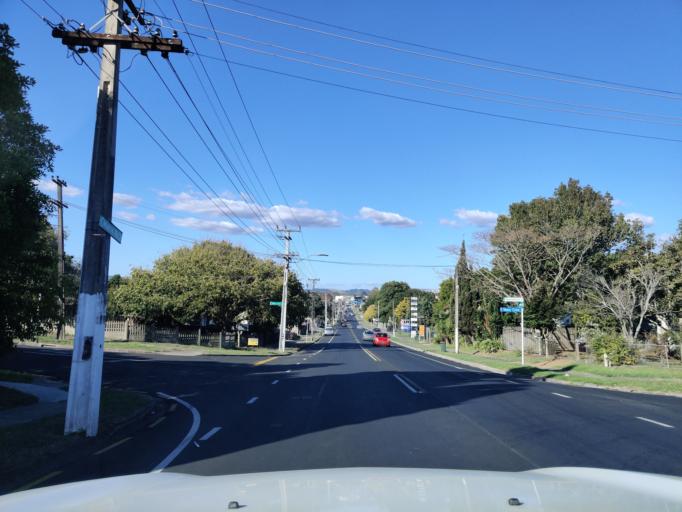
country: NZ
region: Auckland
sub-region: Auckland
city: Takanini
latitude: -37.0351
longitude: 174.8983
